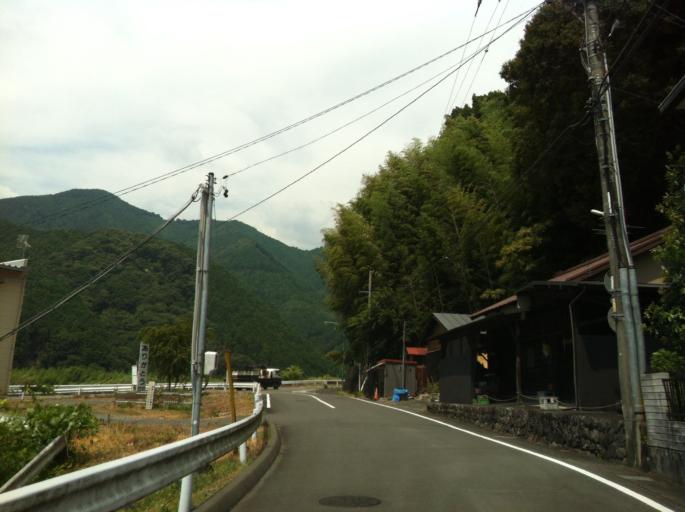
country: JP
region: Shizuoka
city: Shizuoka-shi
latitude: 35.1018
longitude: 138.3683
